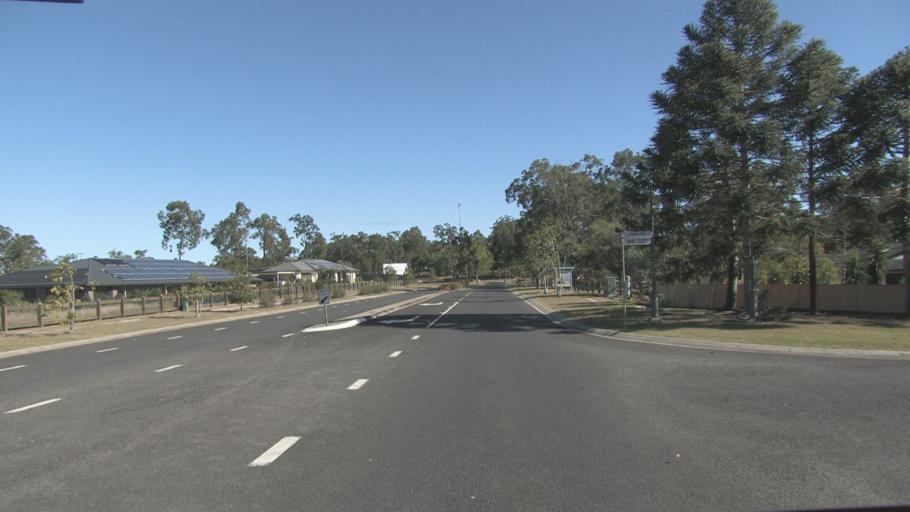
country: AU
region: Queensland
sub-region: Ipswich
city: Springfield Lakes
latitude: -27.7348
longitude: 152.9212
